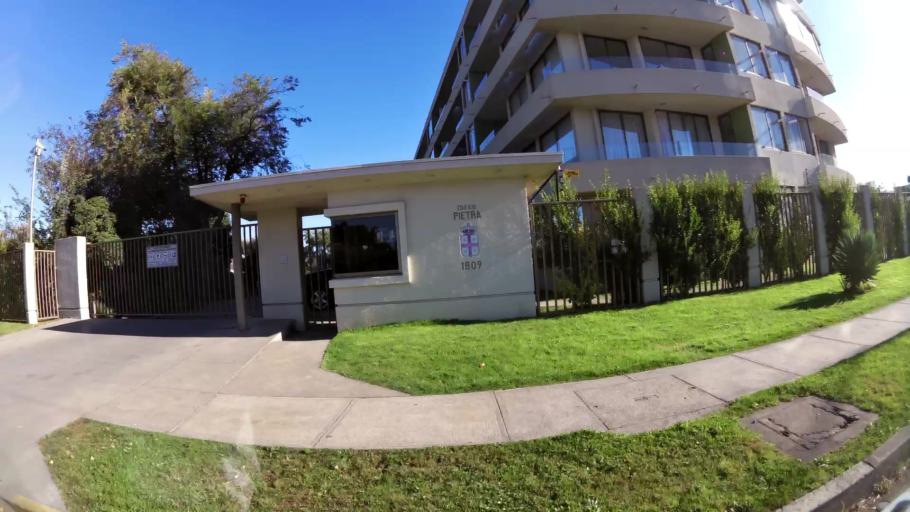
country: CL
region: Biobio
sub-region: Provincia de Concepcion
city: Concepcion
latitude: -36.8367
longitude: -73.1100
